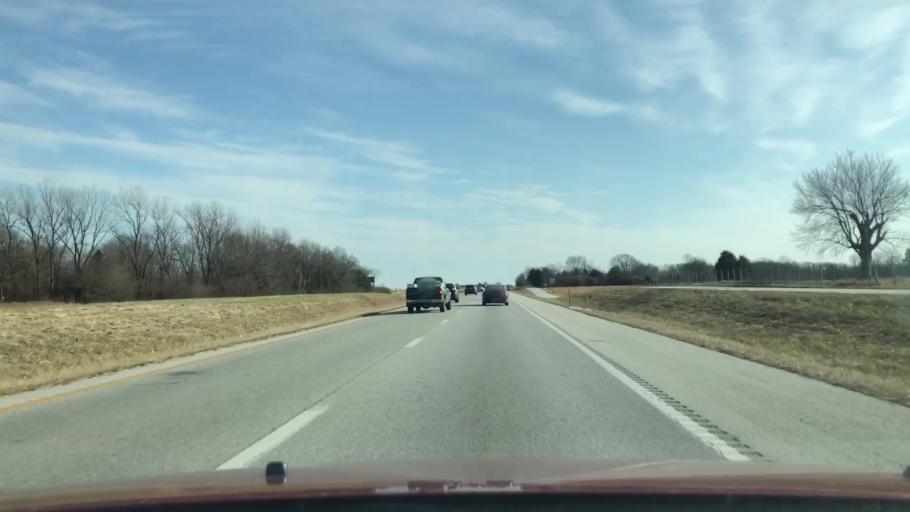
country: US
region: Missouri
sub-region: Webster County
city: Rogersville
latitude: 37.1182
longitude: -93.1008
